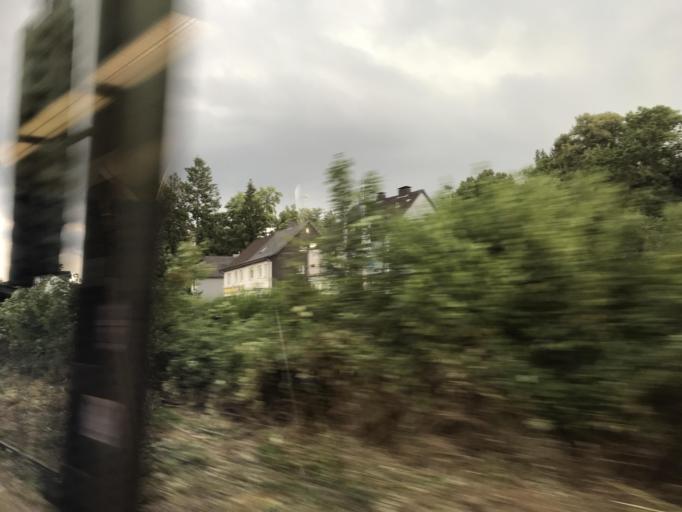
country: DE
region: North Rhine-Westphalia
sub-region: Regierungsbezirk Koln
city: Eitorf
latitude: 50.7740
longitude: 7.4448
